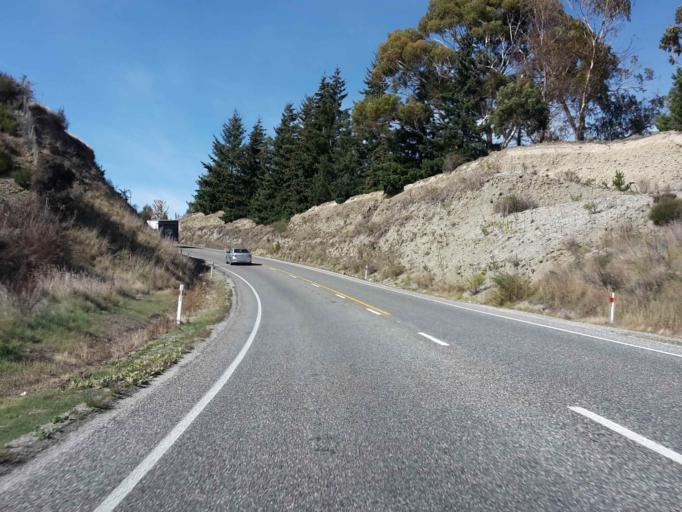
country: NZ
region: Otago
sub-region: Queenstown-Lakes District
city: Wanaka
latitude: -44.7000
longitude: 169.1787
